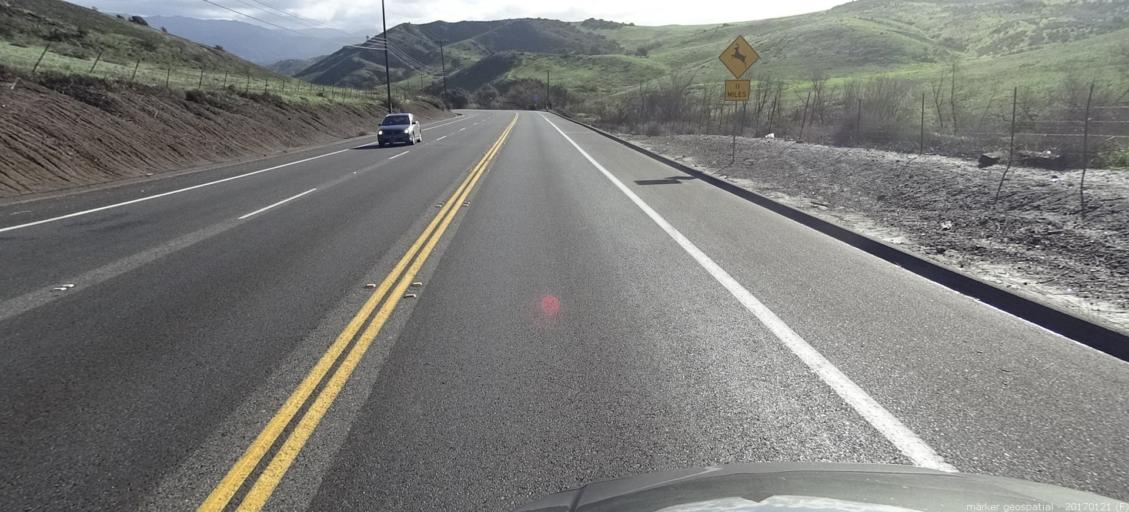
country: US
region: California
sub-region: Orange County
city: North Tustin
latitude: 33.7683
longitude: -117.7325
